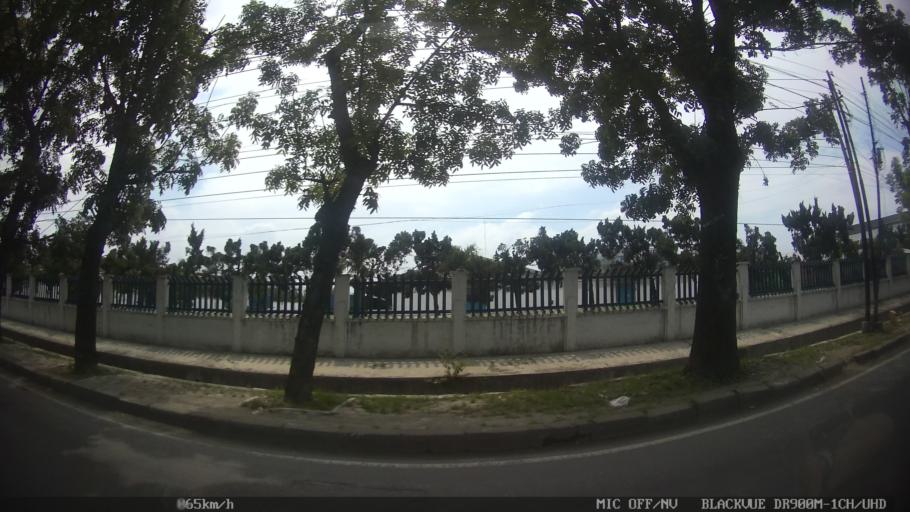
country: ID
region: North Sumatra
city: Medan
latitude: 3.6508
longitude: 98.6632
